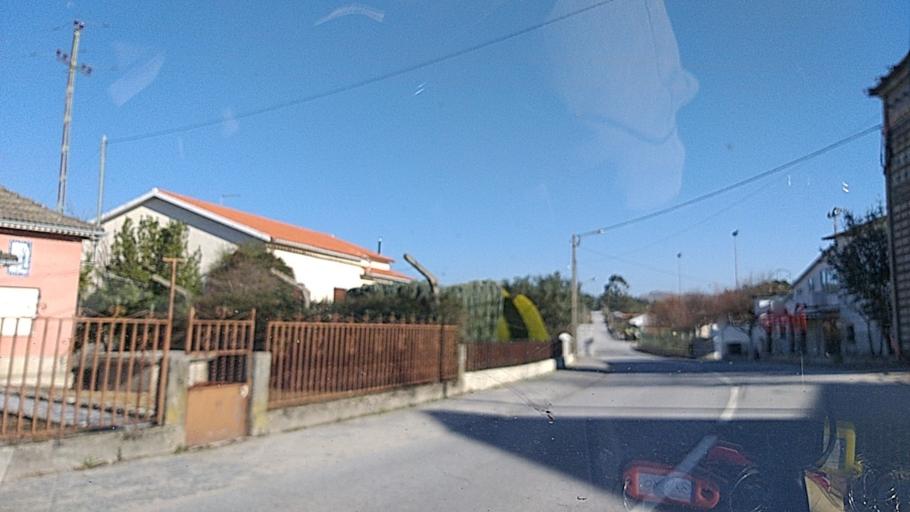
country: PT
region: Guarda
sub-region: Fornos de Algodres
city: Fornos de Algodres
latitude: 40.6321
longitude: -7.4980
